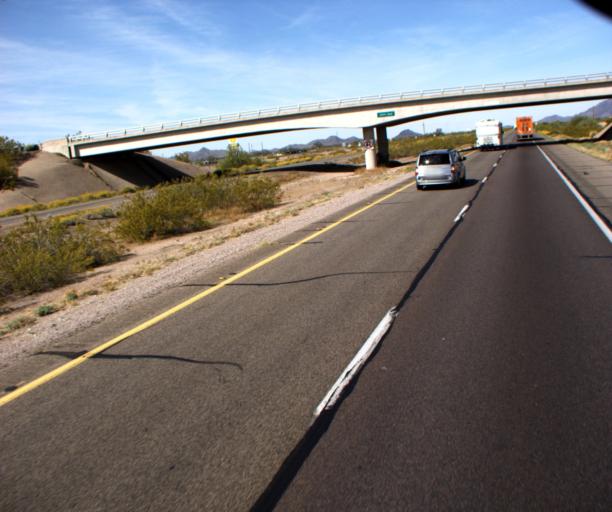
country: US
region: Arizona
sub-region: Maricopa County
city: Buckeye
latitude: 33.4973
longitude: -112.9361
